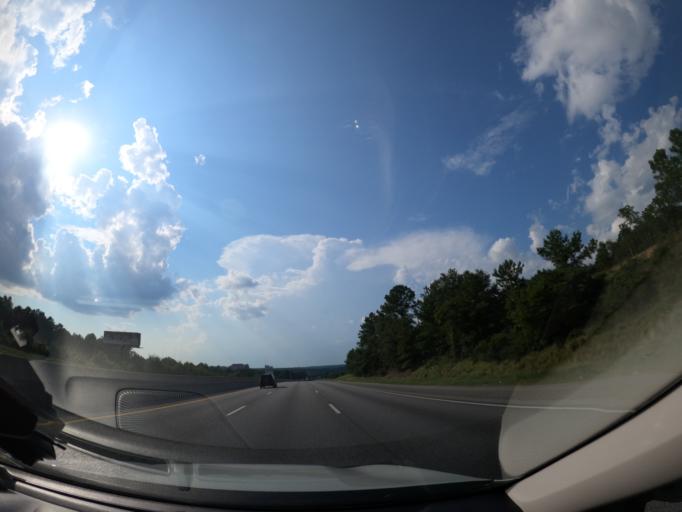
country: US
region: Georgia
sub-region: Columbia County
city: Martinez
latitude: 33.4304
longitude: -82.0664
